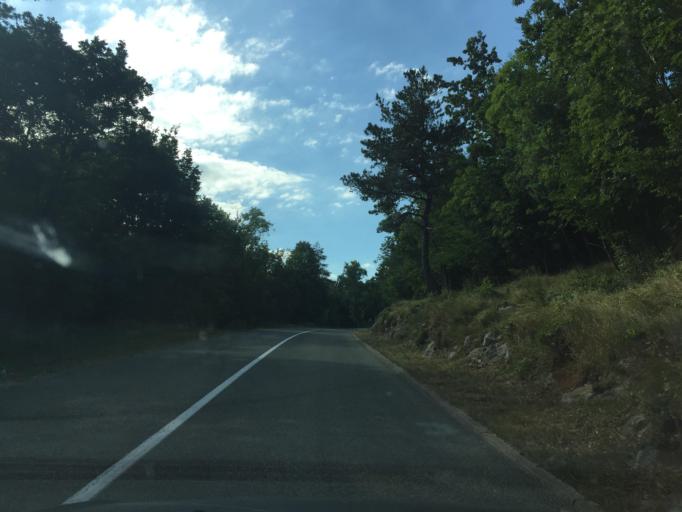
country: HR
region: Primorsko-Goranska
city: Klana
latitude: 45.4478
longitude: 14.3245
